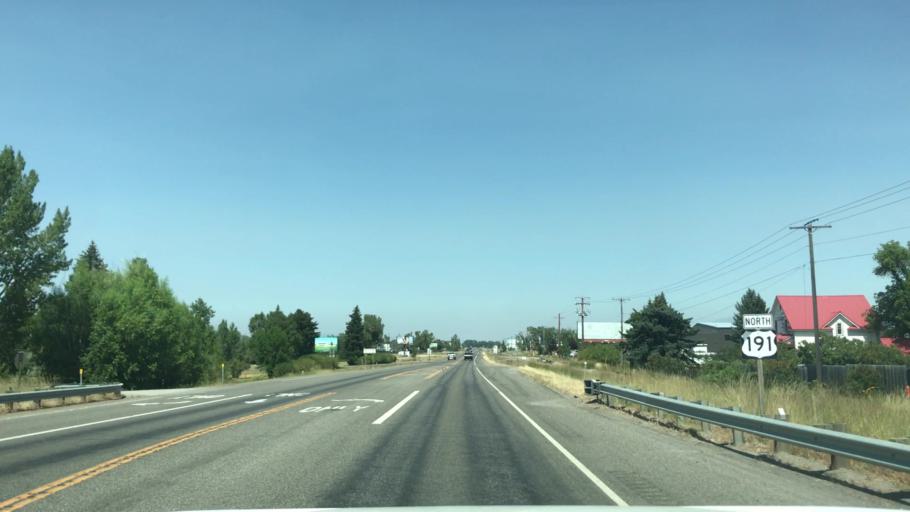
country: US
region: Montana
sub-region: Gallatin County
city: Four Corners
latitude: 45.5918
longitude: -111.1970
